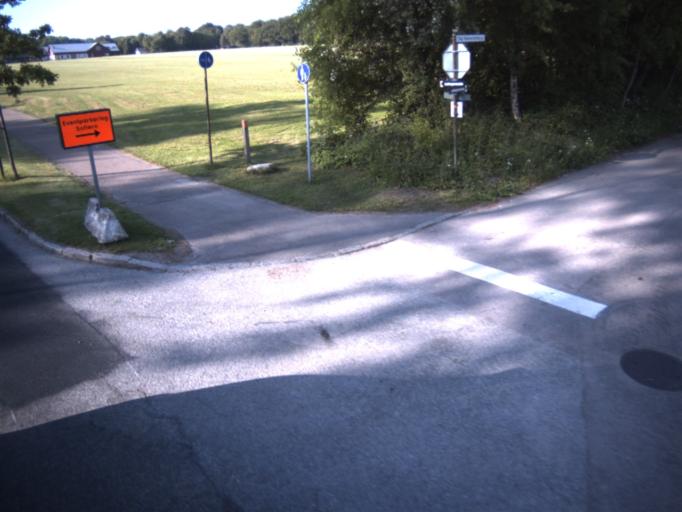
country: SE
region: Skane
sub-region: Helsingborg
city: Helsingborg
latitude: 56.0798
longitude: 12.6639
